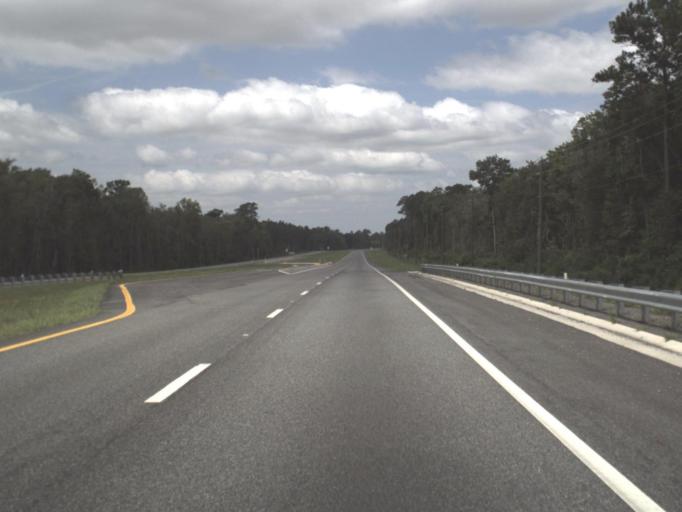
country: US
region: Florida
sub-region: Nassau County
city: Callahan
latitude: 30.6082
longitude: -81.7424
